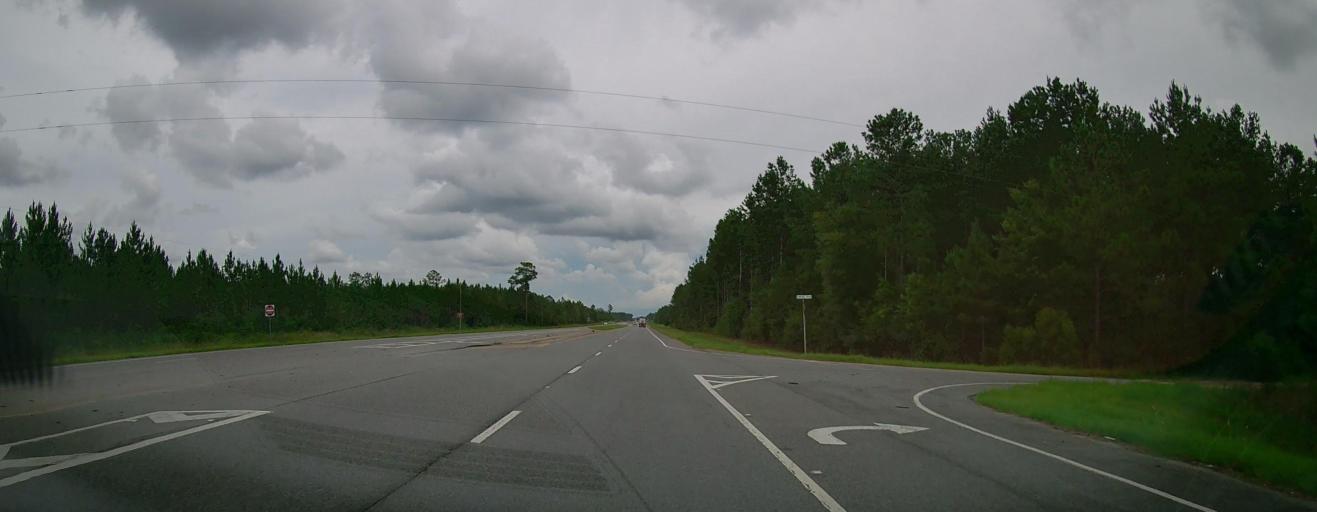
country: US
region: Georgia
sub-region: Wayne County
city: Jesup
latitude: 31.6784
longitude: -82.0835
